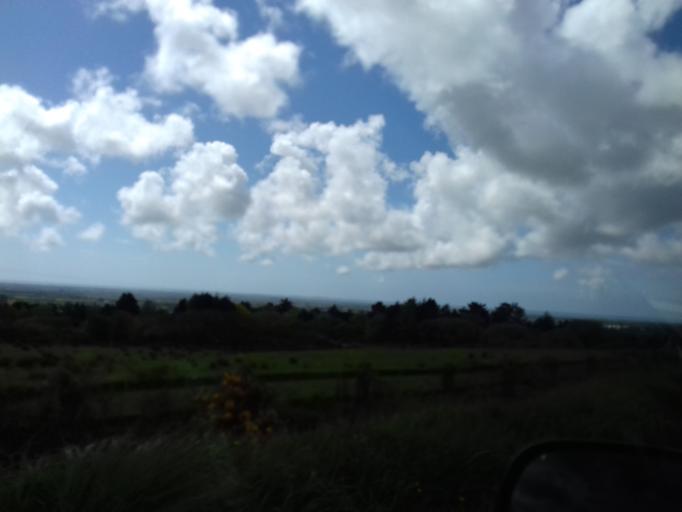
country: IE
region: Leinster
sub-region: Loch Garman
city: Loch Garman
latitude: 52.2967
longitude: -6.5692
